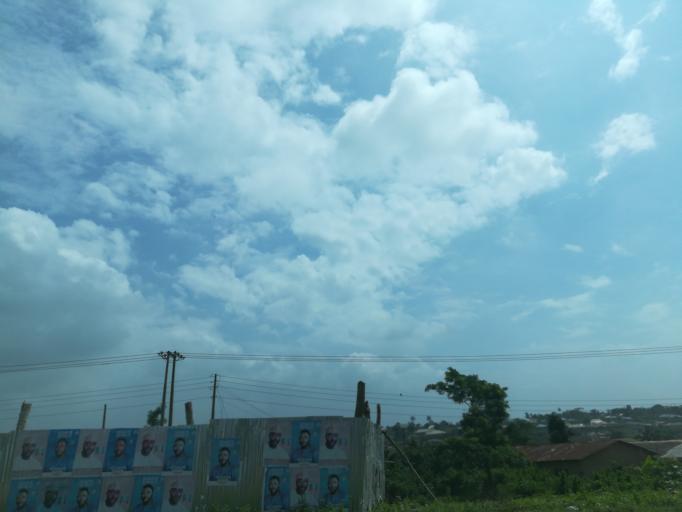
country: NG
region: Lagos
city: Ikorodu
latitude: 6.6664
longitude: 3.6747
